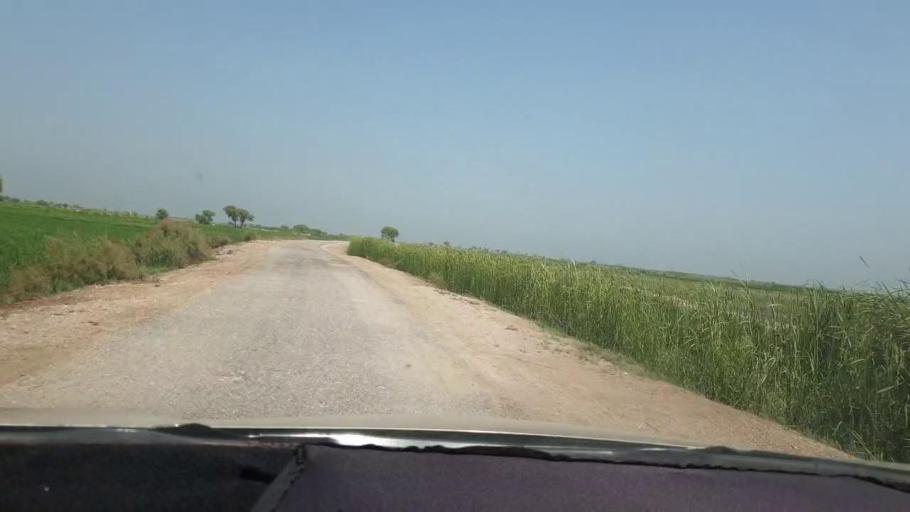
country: PK
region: Sindh
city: Shahdadkot
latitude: 27.8312
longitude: 67.9909
